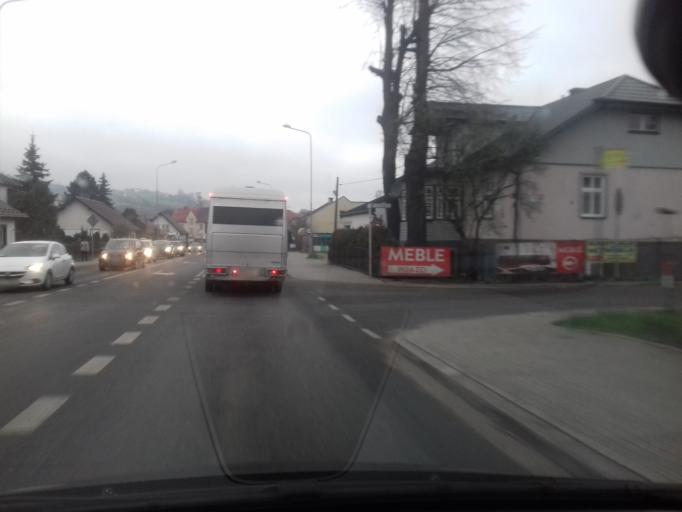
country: PL
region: Lesser Poland Voivodeship
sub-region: Powiat limanowski
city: Limanowa
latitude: 49.7211
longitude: 20.4064
